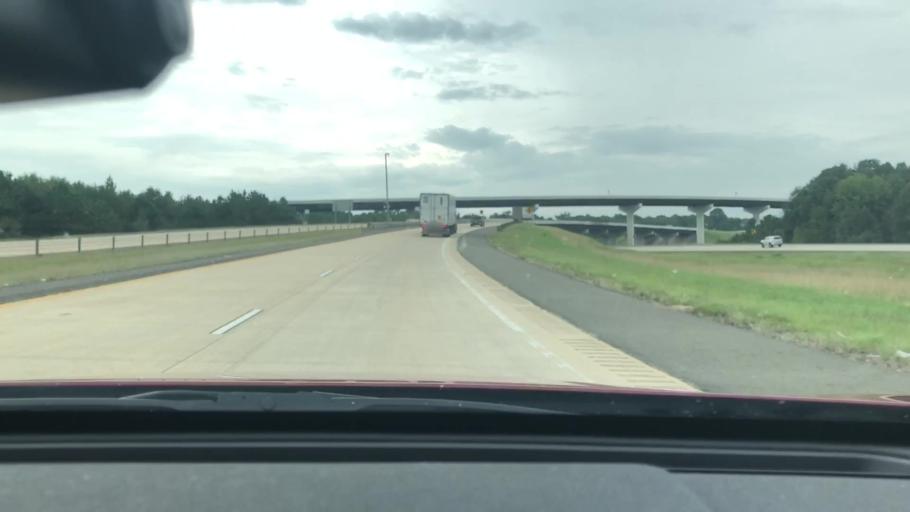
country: US
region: Texas
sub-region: Bowie County
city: Texarkana
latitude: 33.3889
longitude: -94.0177
